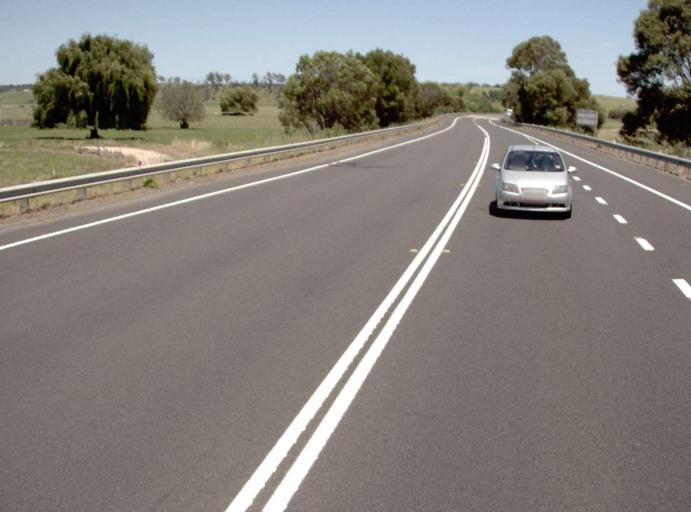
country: AU
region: Victoria
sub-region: East Gippsland
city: Lakes Entrance
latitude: -37.7186
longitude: 148.4524
